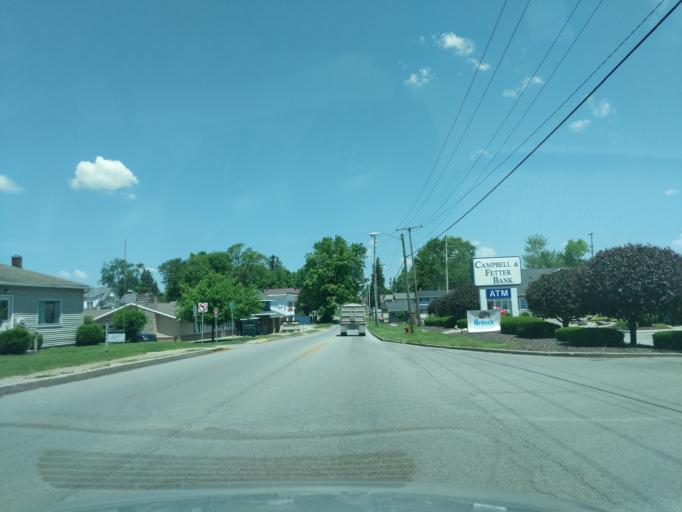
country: US
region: Indiana
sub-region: Noble County
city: Ligonier
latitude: 41.4578
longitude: -85.5866
